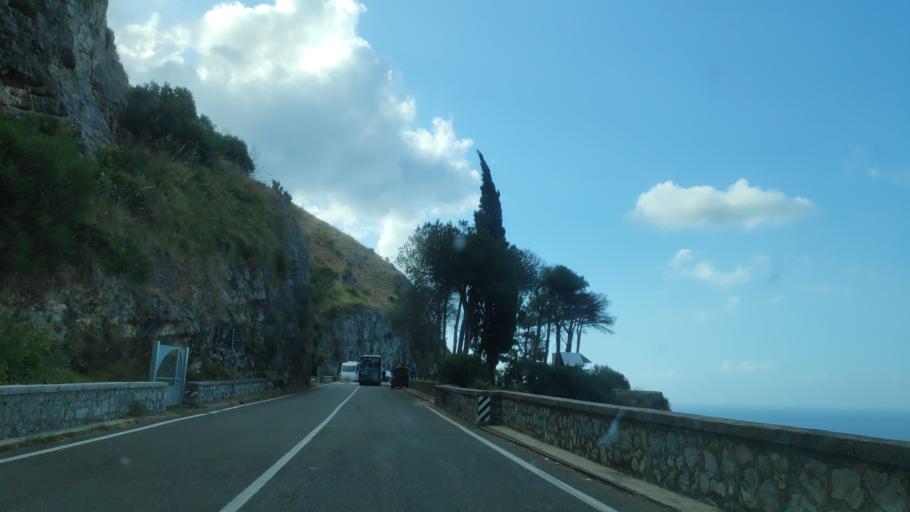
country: IT
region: Campania
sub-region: Provincia di Salerno
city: Positano
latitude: 40.6209
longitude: 14.4585
